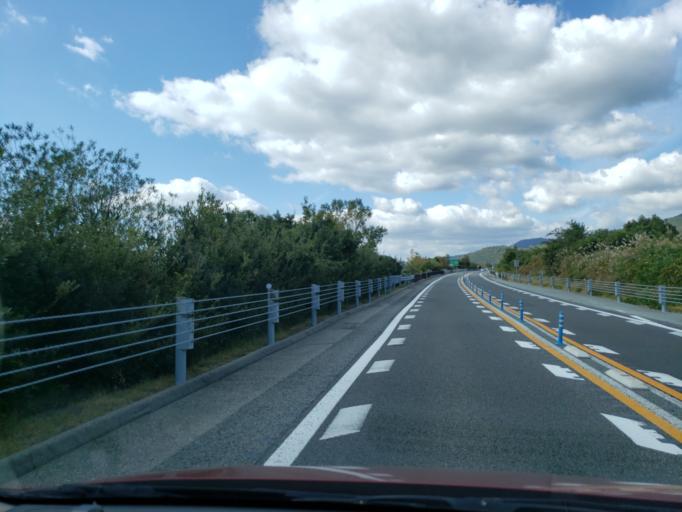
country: JP
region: Tokushima
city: Kamojimacho-jogejima
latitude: 34.1213
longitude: 134.3715
